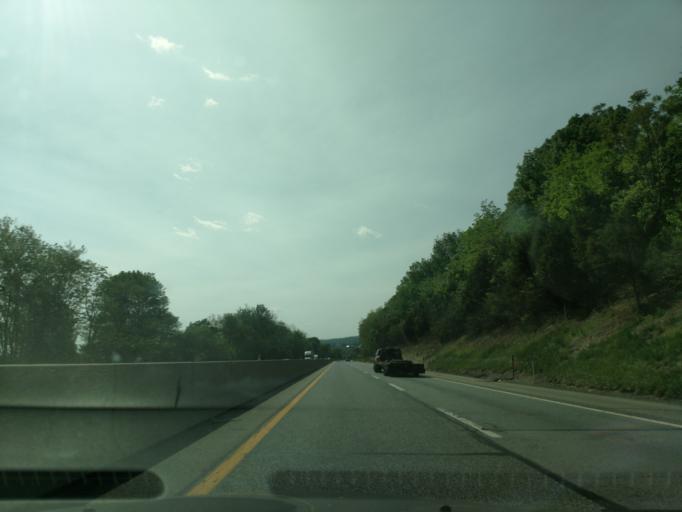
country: US
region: Pennsylvania
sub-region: Lancaster County
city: Denver
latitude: 40.2301
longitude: -76.1212
